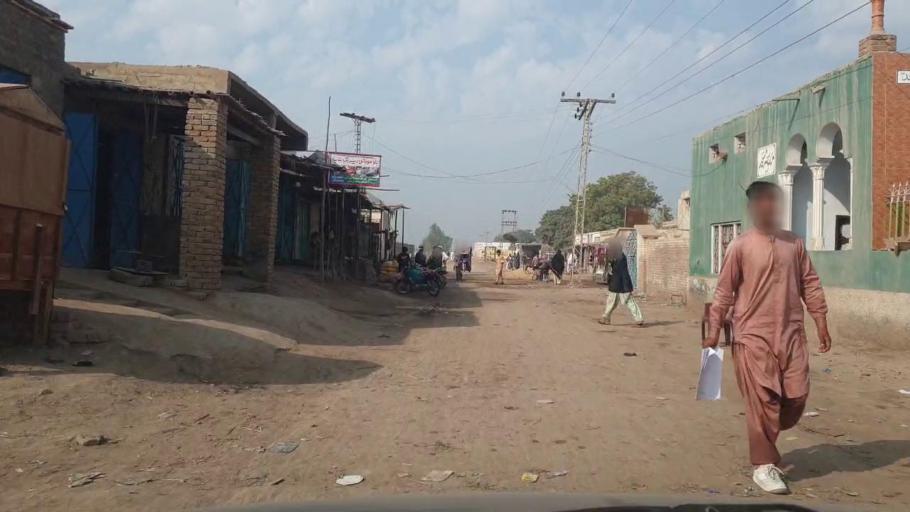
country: PK
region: Sindh
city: Hala
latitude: 25.9045
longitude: 68.4275
